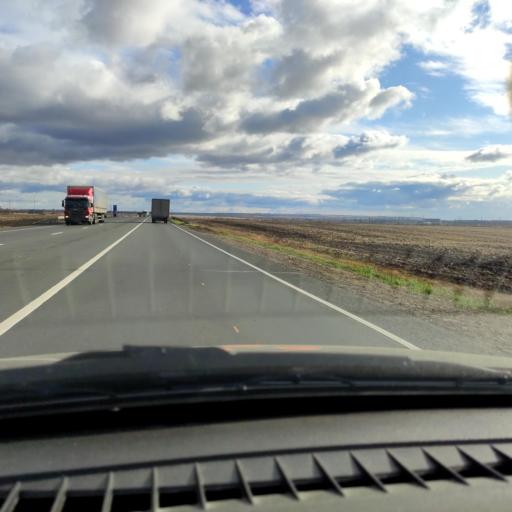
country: RU
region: Samara
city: Varlamovo
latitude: 53.2118
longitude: 48.4512
